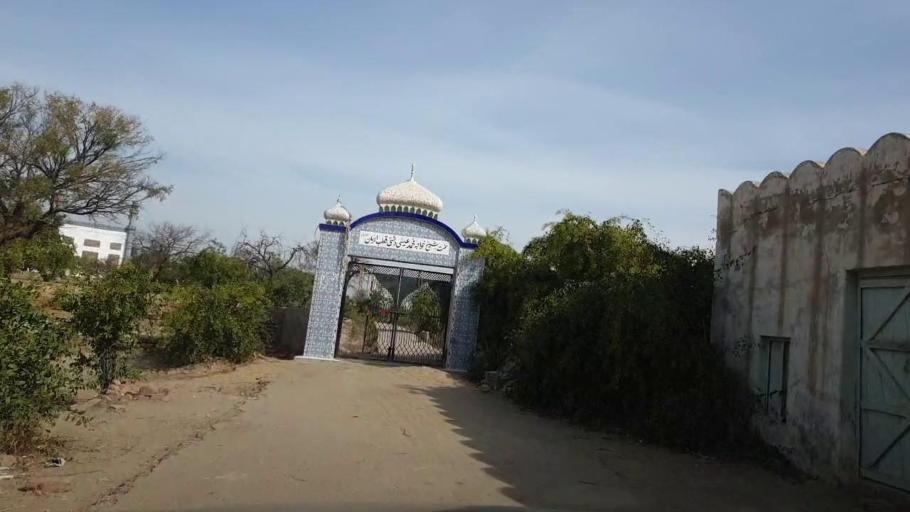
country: PK
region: Sindh
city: Kunri
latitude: 25.1585
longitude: 69.6555
